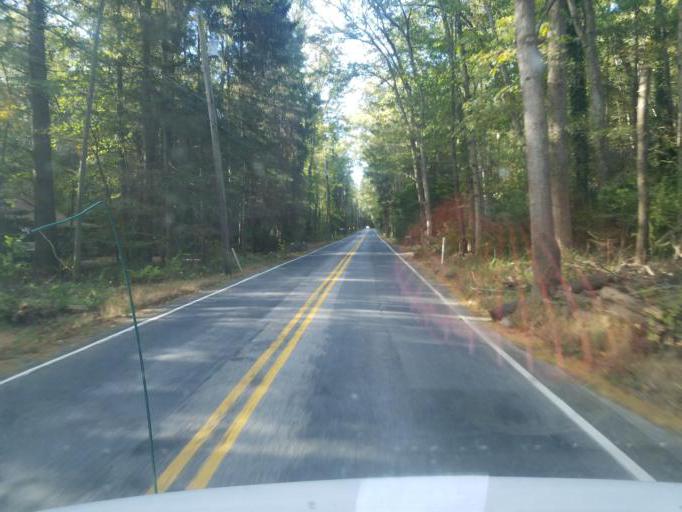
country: US
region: Pennsylvania
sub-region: Franklin County
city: Fayetteville
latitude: 39.9037
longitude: -77.4788
